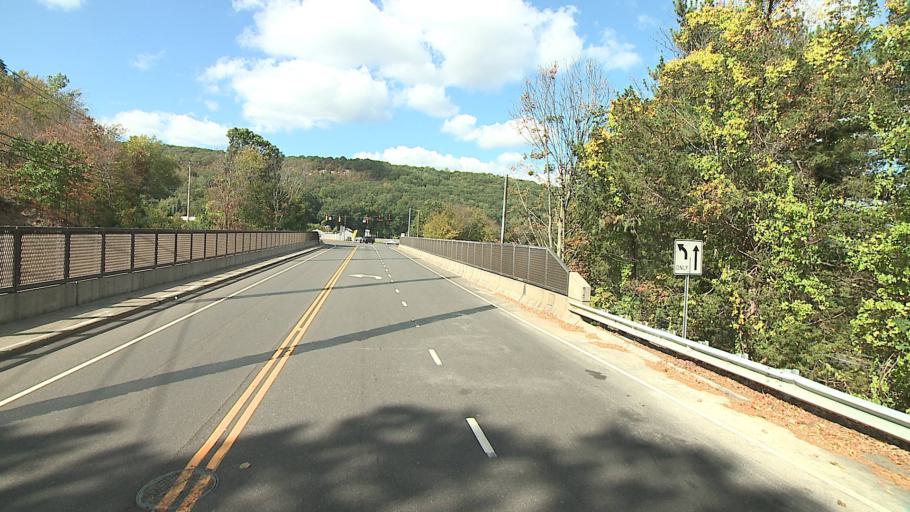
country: US
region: Connecticut
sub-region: New Haven County
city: Ansonia
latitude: 41.3591
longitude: -73.0923
